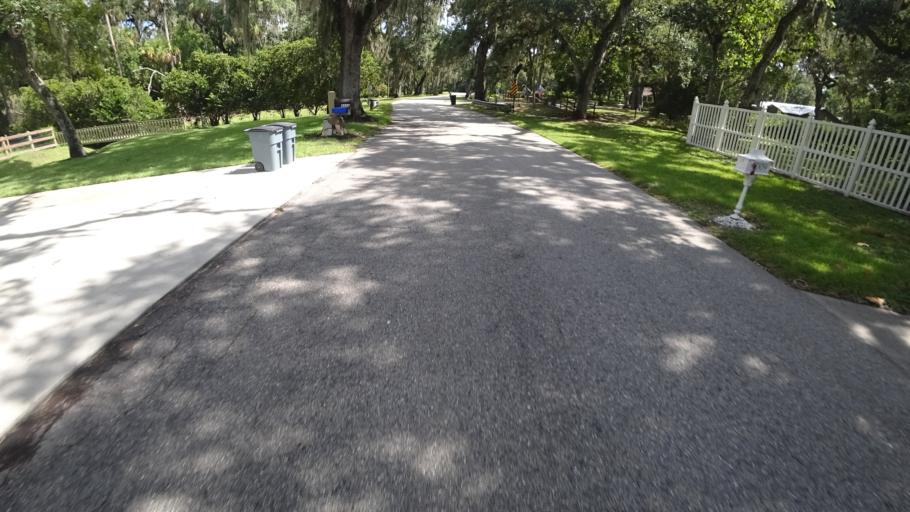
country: US
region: Florida
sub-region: Manatee County
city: Samoset
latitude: 27.4634
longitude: -82.4785
